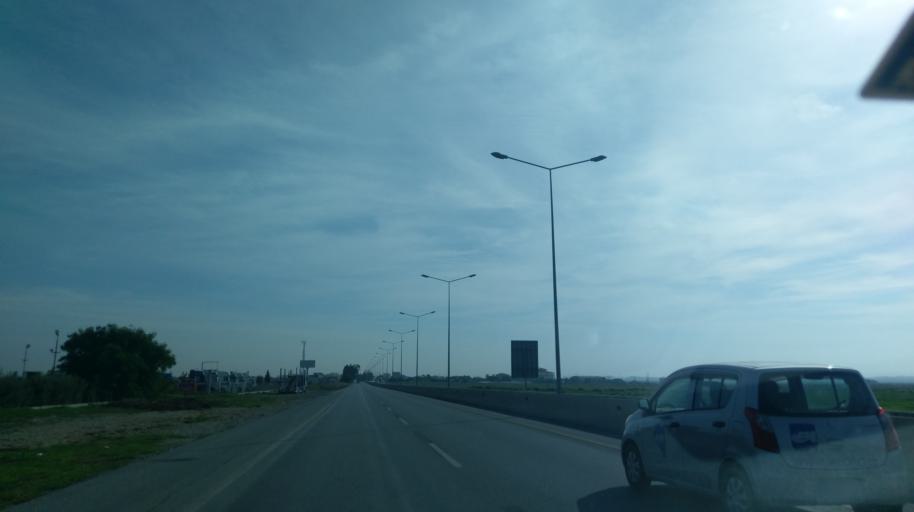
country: CY
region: Lefkosia
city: Geri
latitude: 35.2175
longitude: 33.5034
